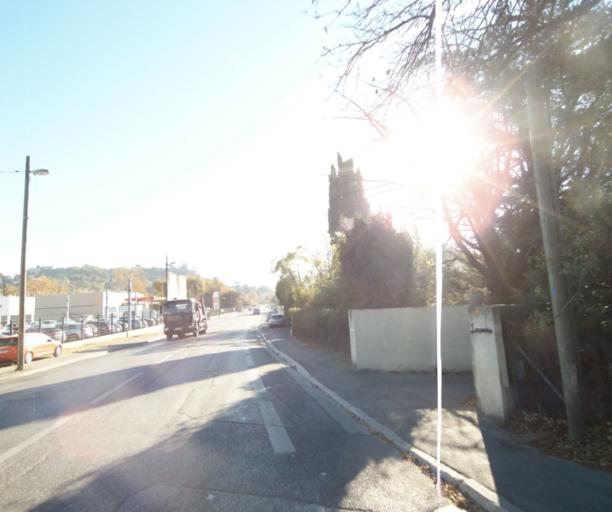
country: FR
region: Provence-Alpes-Cote d'Azur
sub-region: Departement des Bouches-du-Rhone
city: Marseille 11
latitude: 43.2925
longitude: 5.4581
